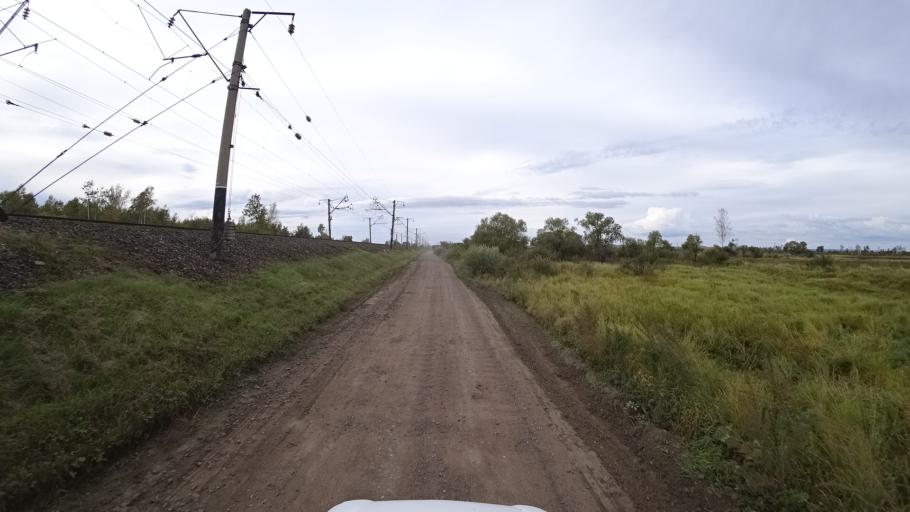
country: RU
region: Amur
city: Arkhara
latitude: 49.3558
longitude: 130.1542
